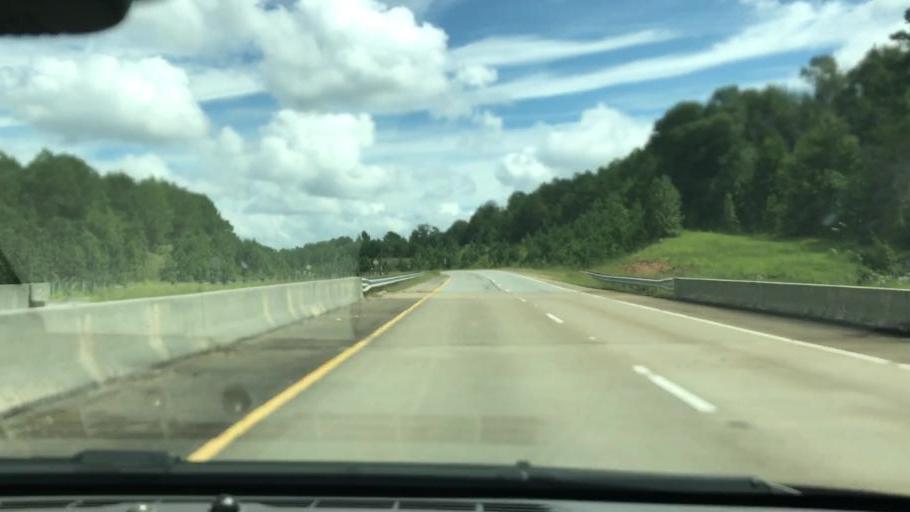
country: US
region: Georgia
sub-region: Stewart County
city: Lumpkin
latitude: 32.0591
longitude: -84.7998
